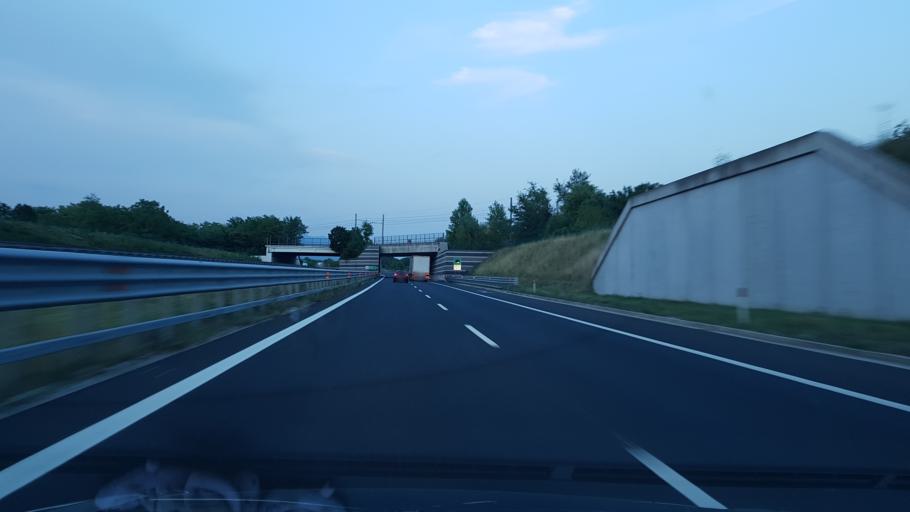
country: IT
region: Friuli Venezia Giulia
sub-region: Provincia di Gorizia
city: Savogna d'Isonzo
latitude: 45.9045
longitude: 13.5798
